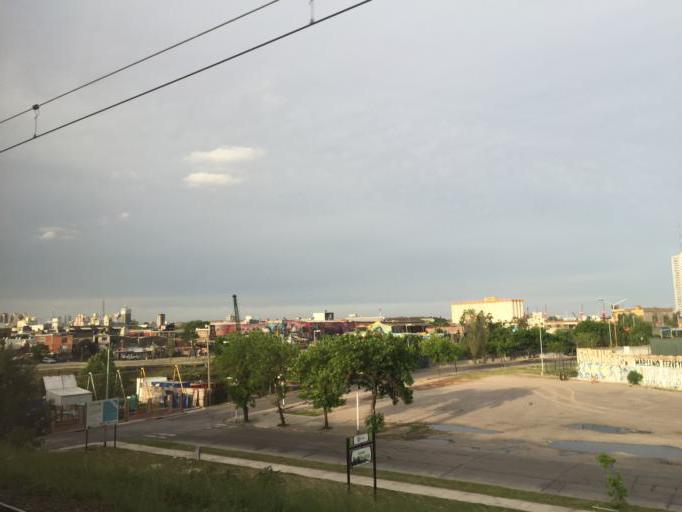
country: AR
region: Buenos Aires
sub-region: Partido de Avellaneda
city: Avellaneda
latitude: -34.6584
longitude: -58.3775
